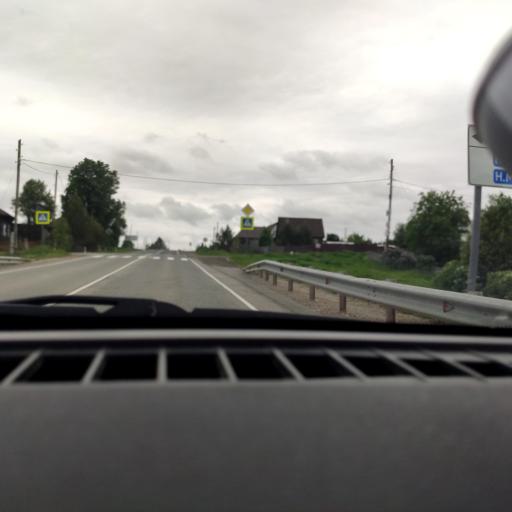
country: RU
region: Perm
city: Ust'-Kachka
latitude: 57.9174
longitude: 55.7663
